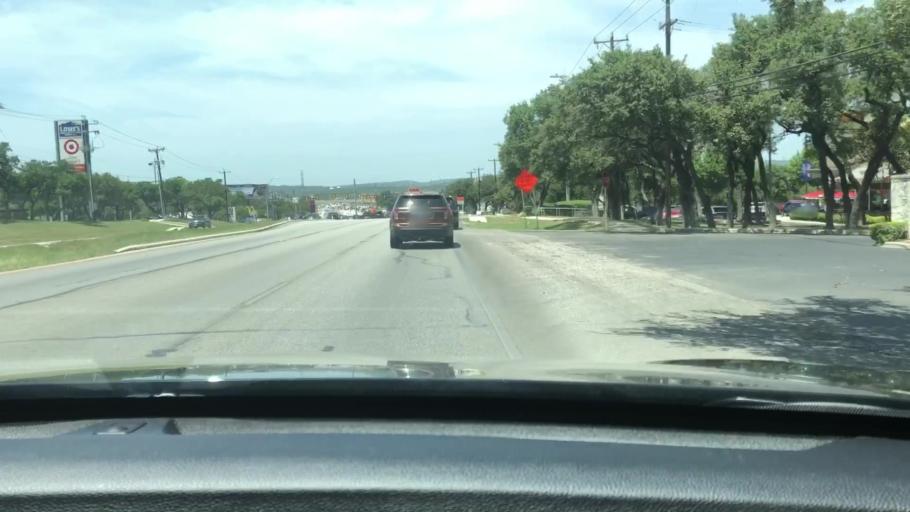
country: US
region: Texas
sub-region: Bexar County
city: Helotes
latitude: 29.5488
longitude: -98.6621
